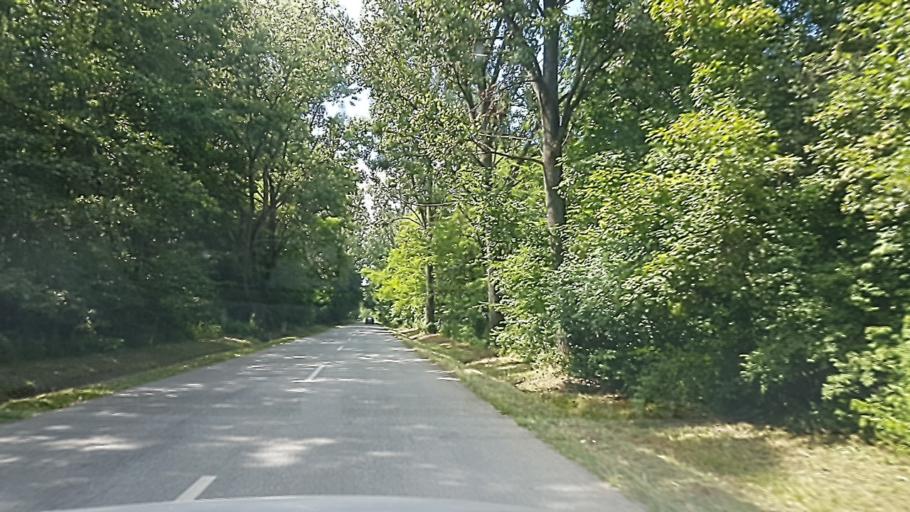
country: HU
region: Somogy
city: Barcs
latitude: 45.9437
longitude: 17.6339
